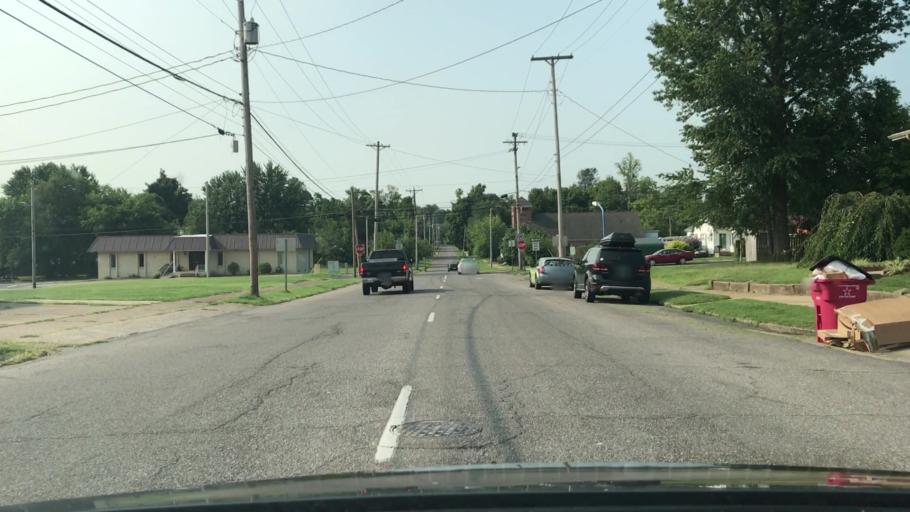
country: US
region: Kentucky
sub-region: Graves County
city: Mayfield
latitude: 36.7391
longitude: -88.6371
